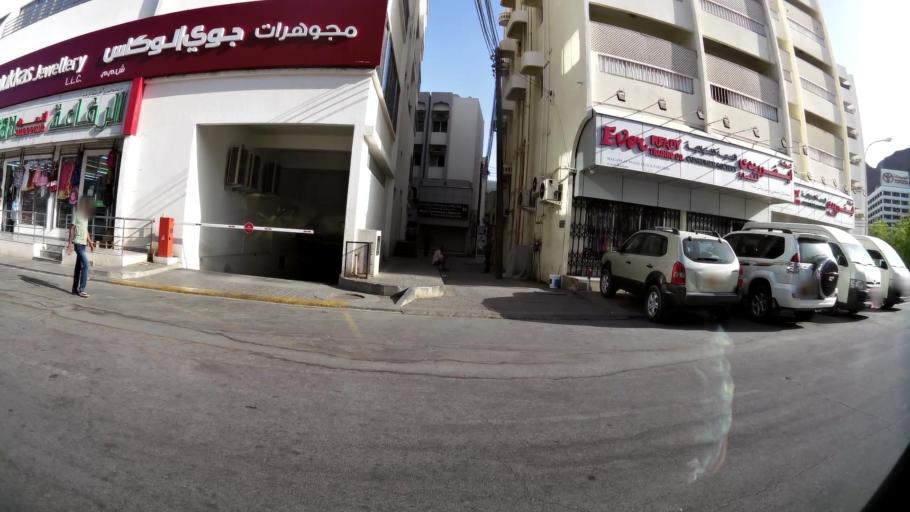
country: OM
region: Muhafazat Masqat
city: Muscat
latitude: 23.5938
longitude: 58.5441
